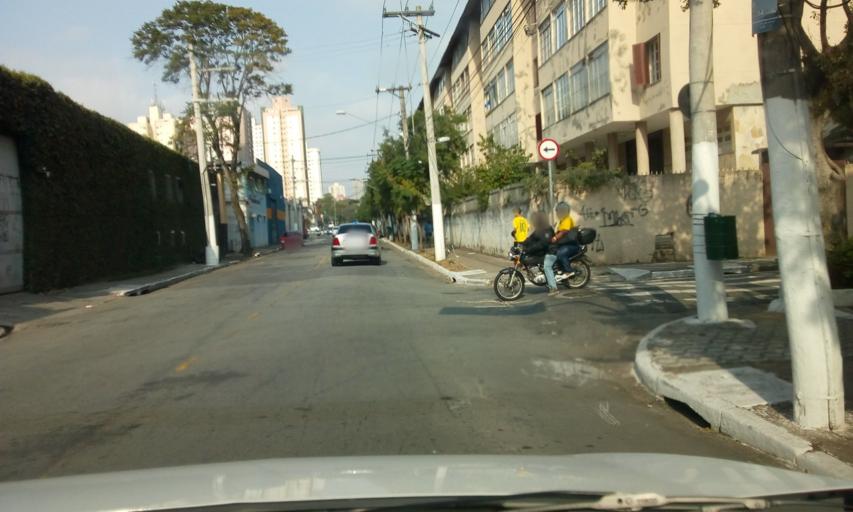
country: BR
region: Sao Paulo
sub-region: Sao Paulo
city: Sao Paulo
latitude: -23.5526
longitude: -46.5929
